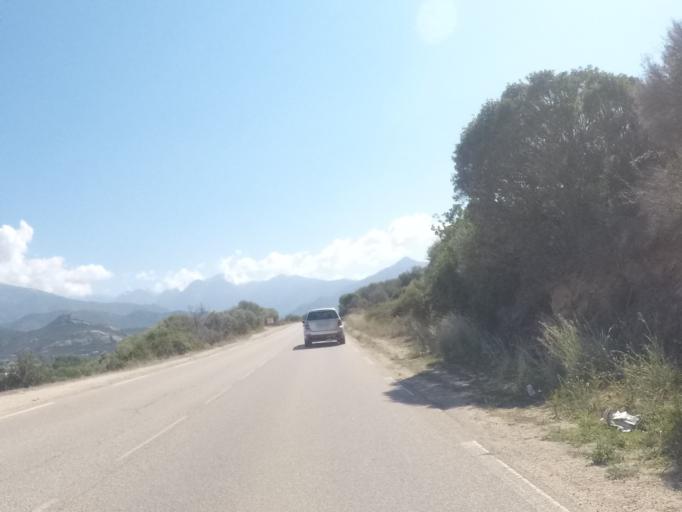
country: FR
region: Corsica
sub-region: Departement de la Haute-Corse
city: Calvi
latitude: 42.5425
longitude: 8.7901
